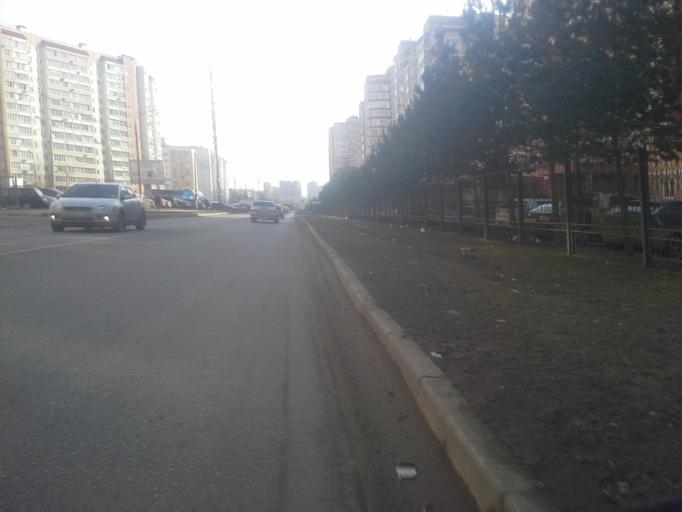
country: RU
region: Moskovskaya
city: Shcherbinka
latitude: 55.4711
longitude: 37.5451
